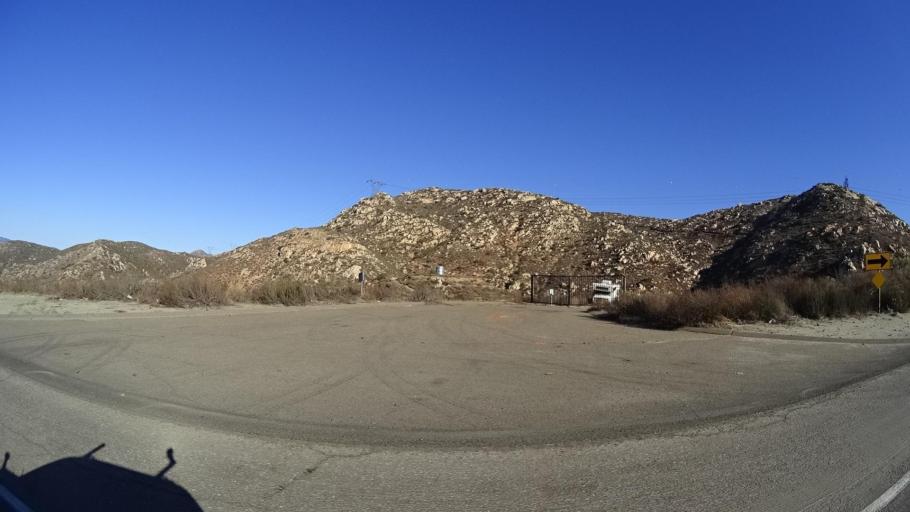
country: MX
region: Baja California
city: Tecate
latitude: 32.5973
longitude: -116.6493
